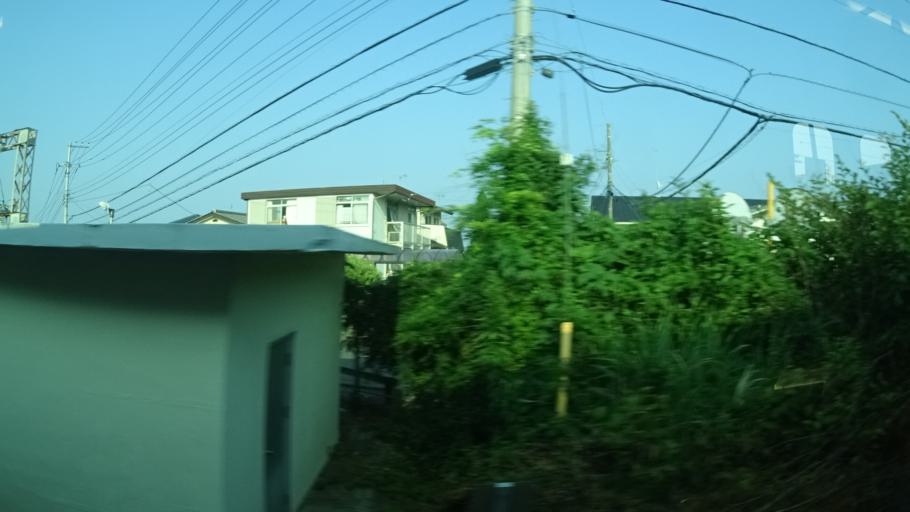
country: JP
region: Ibaraki
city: Hitachi
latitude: 36.6066
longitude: 140.6677
